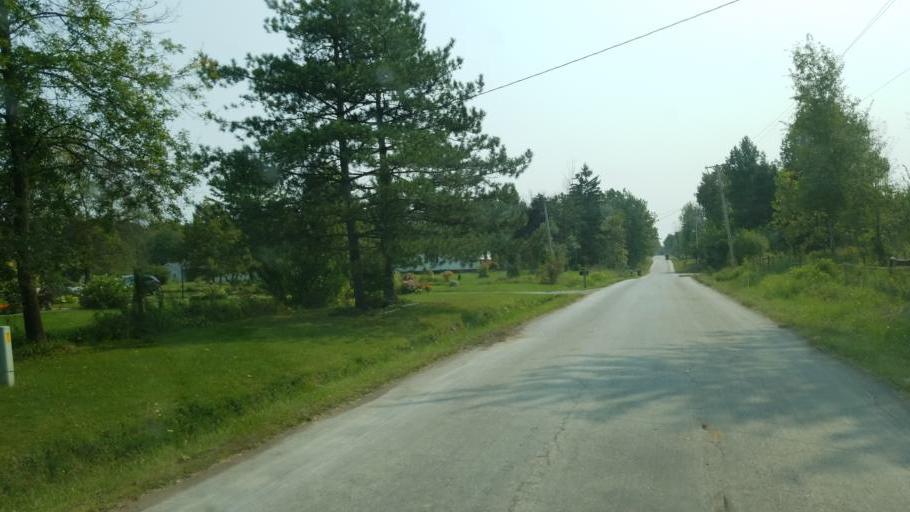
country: US
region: Ohio
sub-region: Geauga County
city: Middlefield
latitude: 41.5227
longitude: -81.0031
